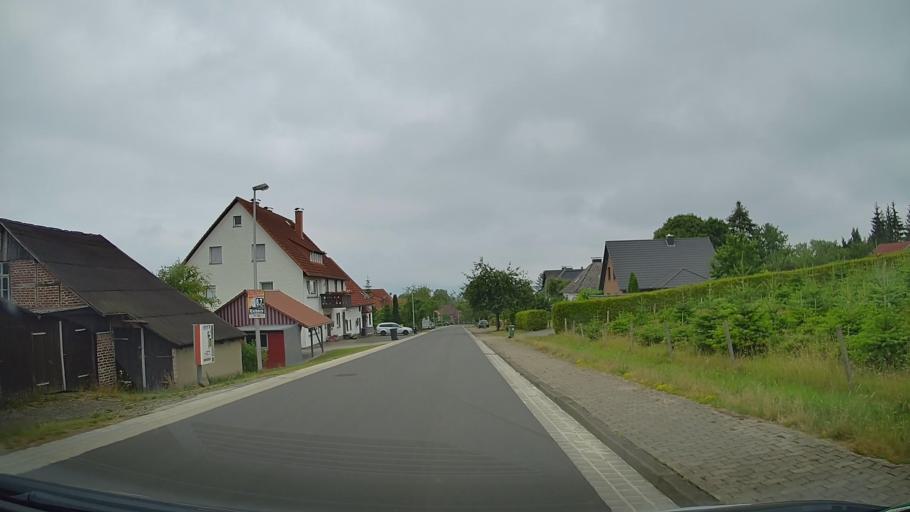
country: DE
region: Lower Saxony
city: Rinteln
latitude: 52.1376
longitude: 9.1005
